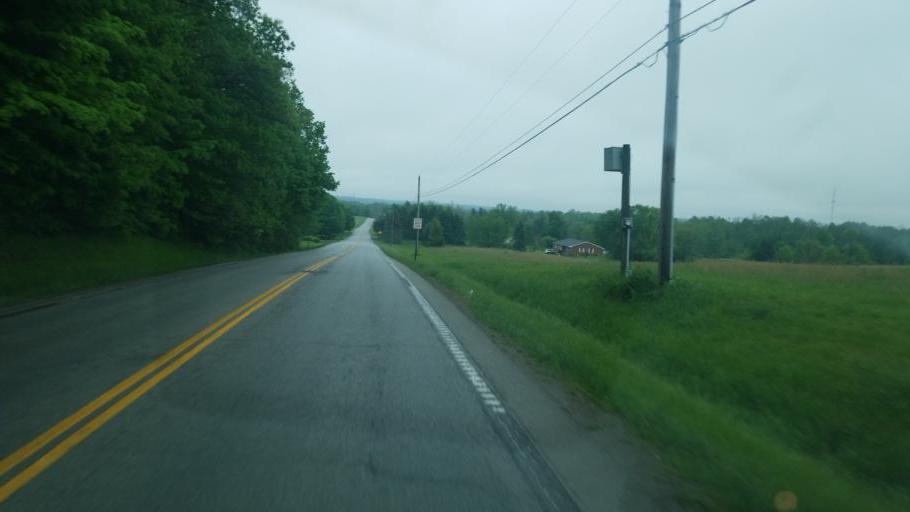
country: US
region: Ohio
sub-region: Highland County
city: Hillsboro
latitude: 39.2605
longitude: -83.5998
